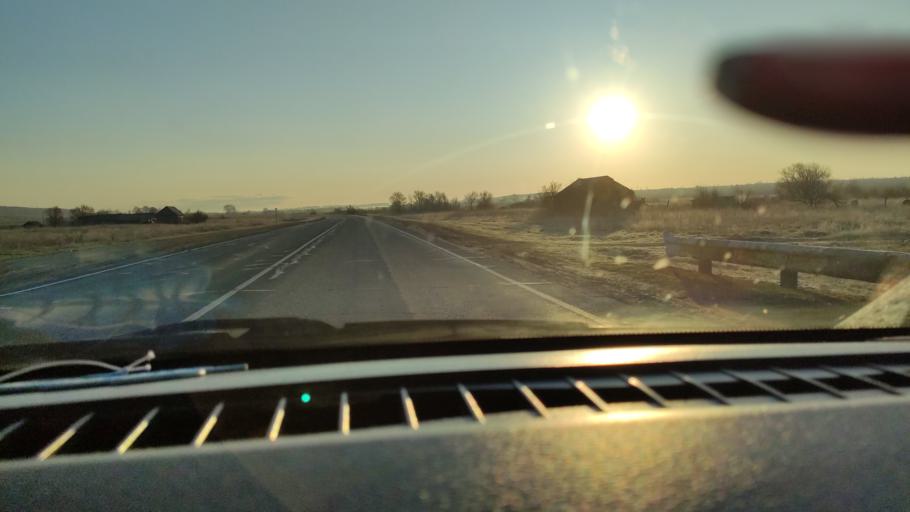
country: RU
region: Saratov
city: Sinodskoye
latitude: 52.0505
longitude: 46.7506
